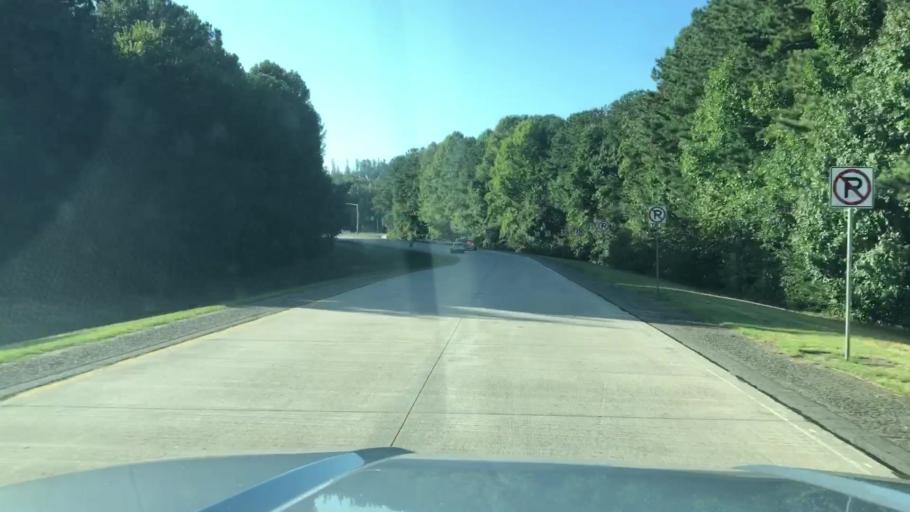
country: US
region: Georgia
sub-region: Cobb County
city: Kennesaw
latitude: 34.0117
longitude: -84.5697
